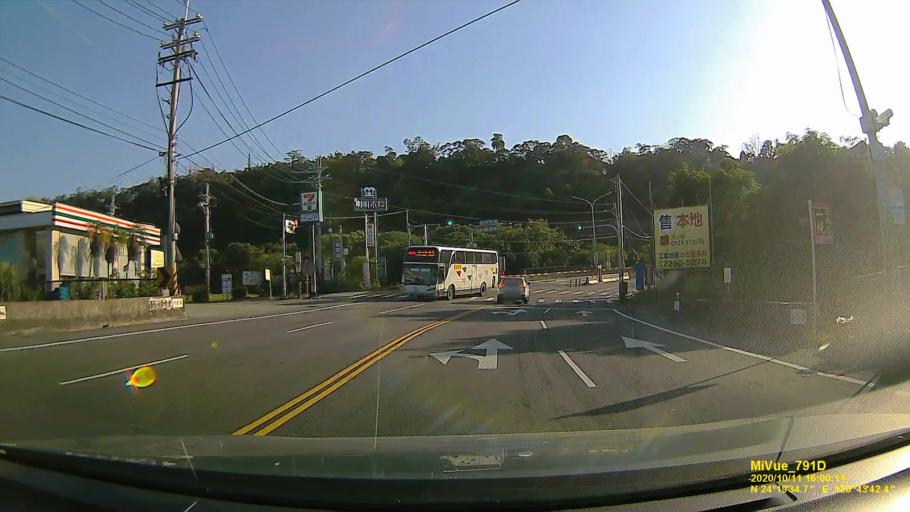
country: TW
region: Taiwan
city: Fengyuan
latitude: 24.3263
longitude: 120.7284
